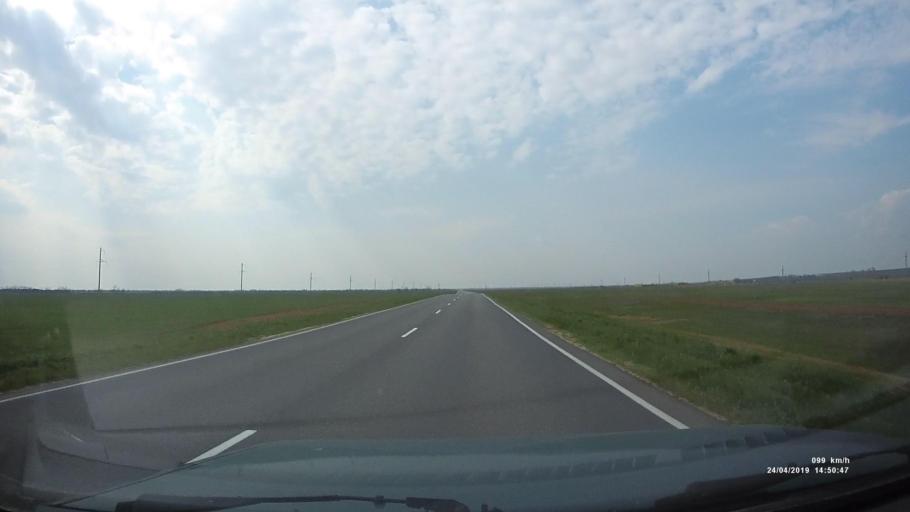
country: RU
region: Rostov
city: Remontnoye
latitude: 46.5199
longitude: 43.7131
